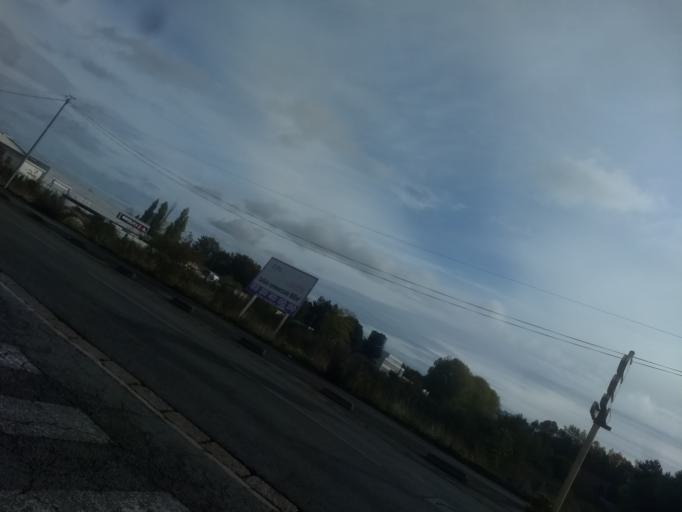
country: FR
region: Nord-Pas-de-Calais
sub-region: Departement du Pas-de-Calais
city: Dainville
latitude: 50.2970
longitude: 2.7310
